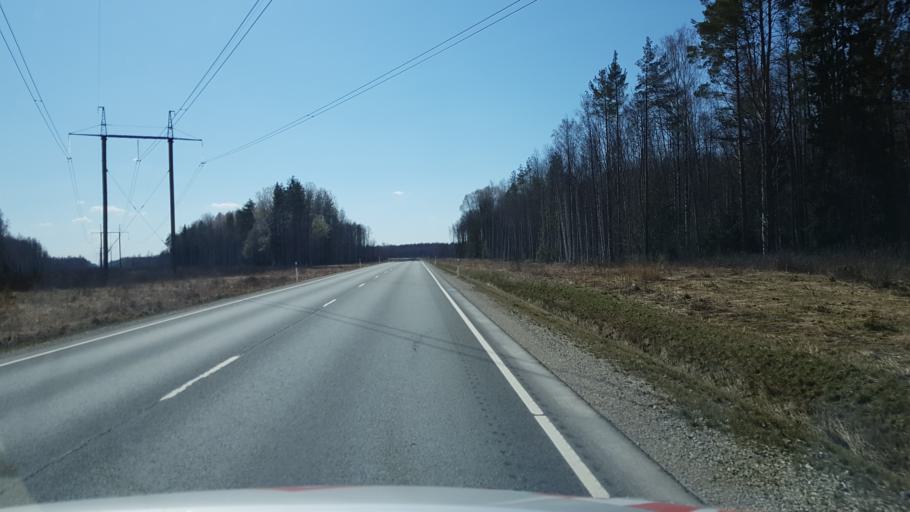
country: EE
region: Jogevamaa
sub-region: Mustvee linn
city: Mustvee
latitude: 58.8607
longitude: 26.9273
